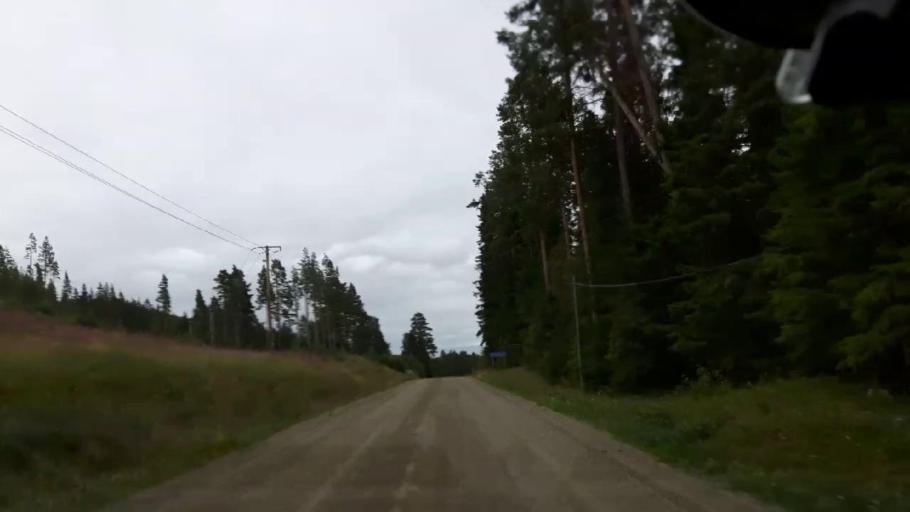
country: SE
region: Jaemtland
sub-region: Braecke Kommun
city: Braecke
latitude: 63.0414
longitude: 15.3578
